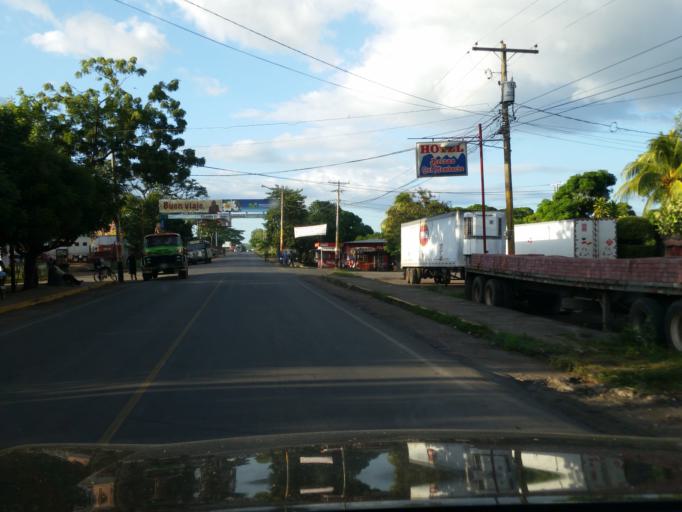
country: NI
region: Granada
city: Nandaime
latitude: 11.7612
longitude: -86.0474
